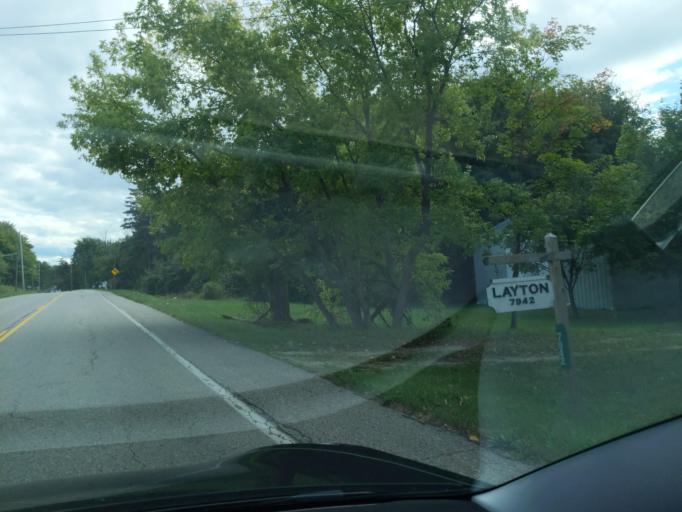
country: US
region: Michigan
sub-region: Kalkaska County
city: Rapid City
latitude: 44.9190
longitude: -85.2856
